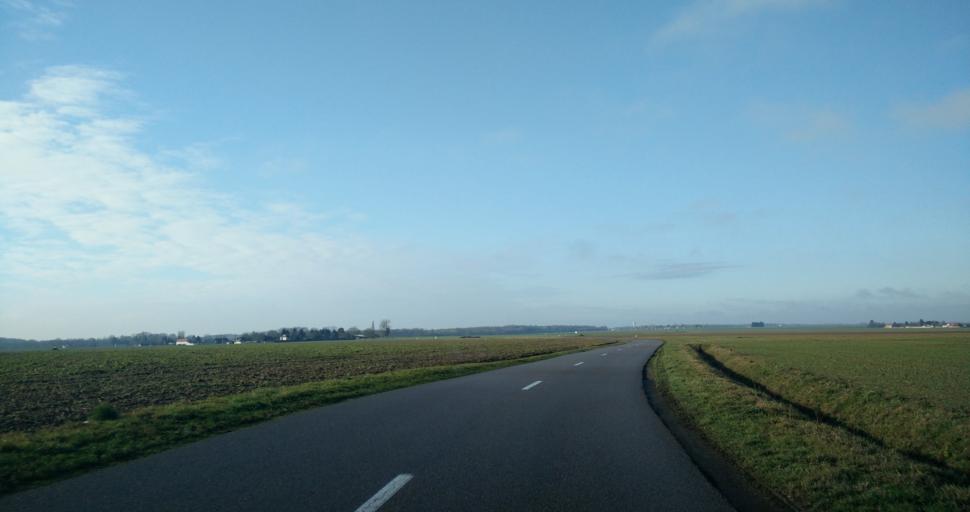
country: FR
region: Haute-Normandie
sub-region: Departement de l'Eure
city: La Haye-Malherbe
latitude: 49.1697
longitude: 1.0842
